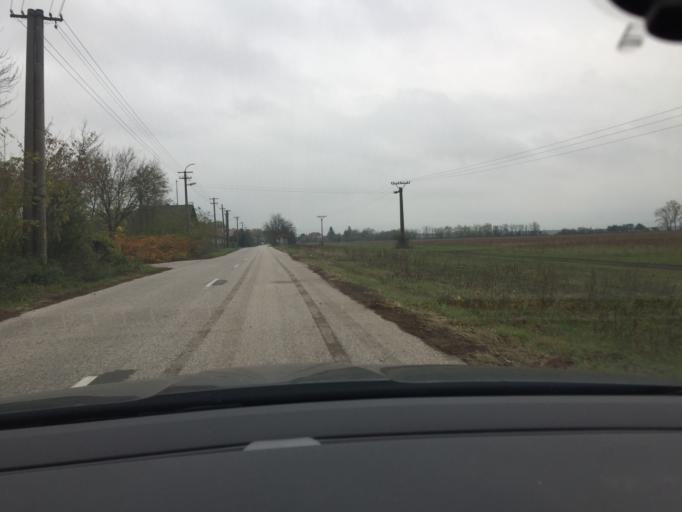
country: HU
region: Komarom-Esztergom
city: Esztergom
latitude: 47.9317
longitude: 18.7470
